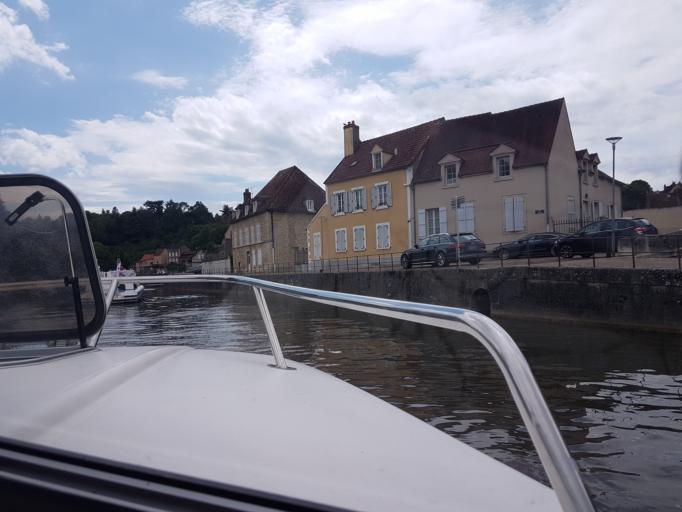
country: FR
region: Bourgogne
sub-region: Departement de la Nievre
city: Clamecy
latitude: 47.4597
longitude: 3.5233
